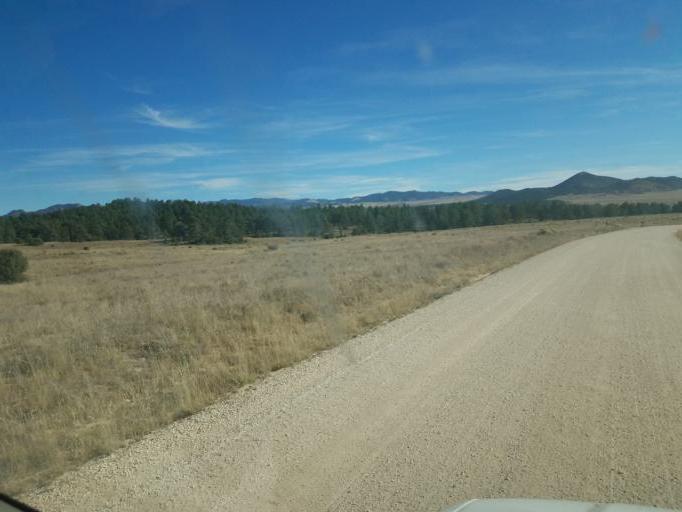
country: US
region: Colorado
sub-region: Custer County
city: Westcliffe
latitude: 38.2312
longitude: -105.4572
